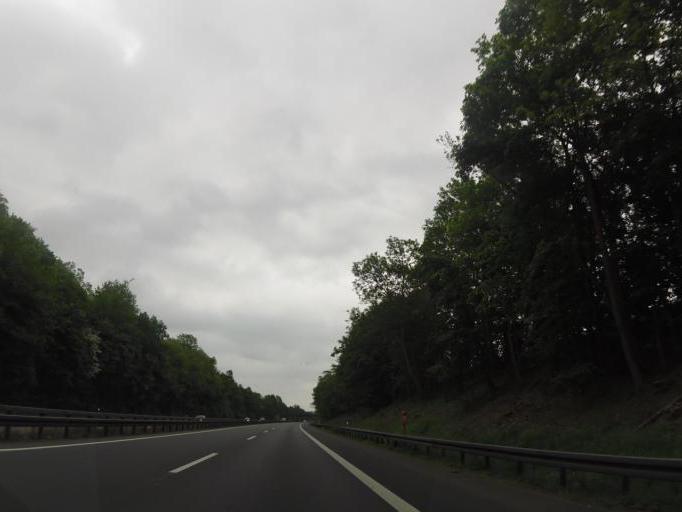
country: DE
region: Lower Saxony
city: Holle
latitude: 52.0954
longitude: 10.1641
